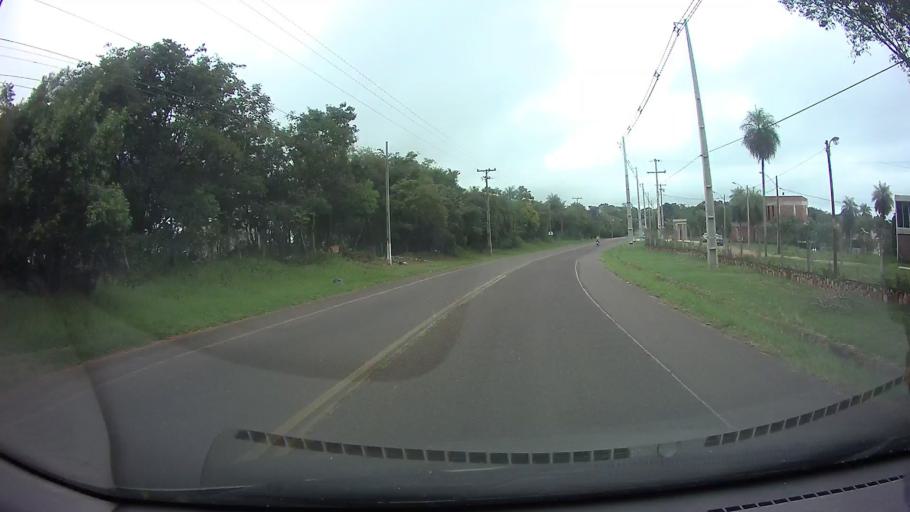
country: PY
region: Cordillera
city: Altos
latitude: -25.2860
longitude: -57.2633
